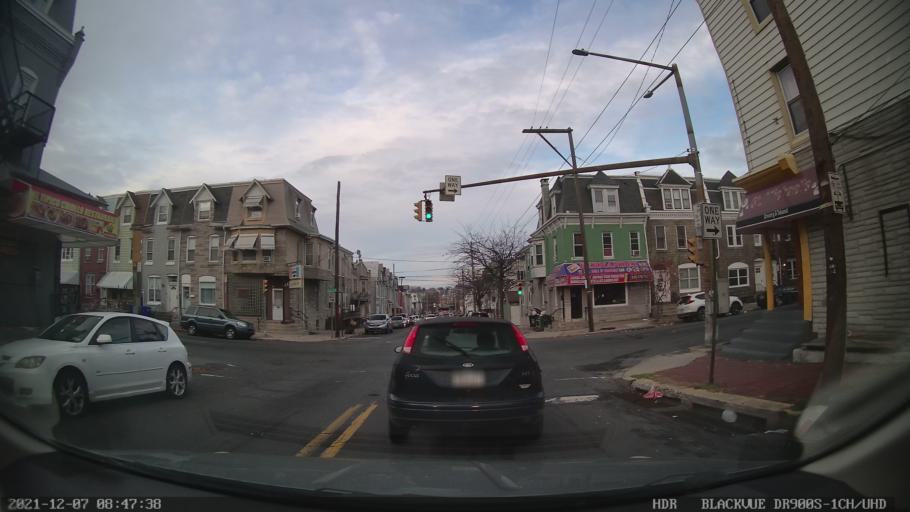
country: US
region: Pennsylvania
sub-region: Berks County
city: Reading
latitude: 40.3503
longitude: -75.9155
